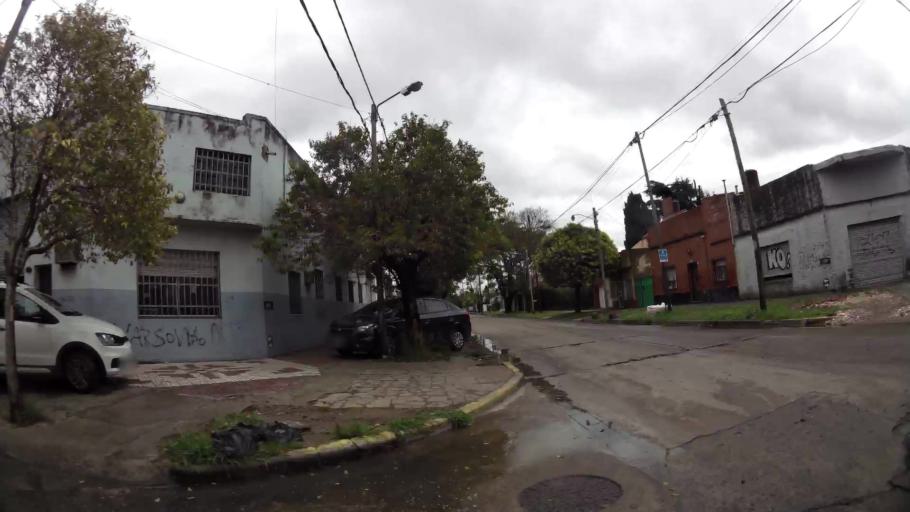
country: AR
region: Buenos Aires
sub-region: Partido de Lomas de Zamora
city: Lomas de Zamora
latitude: -34.7516
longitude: -58.3830
